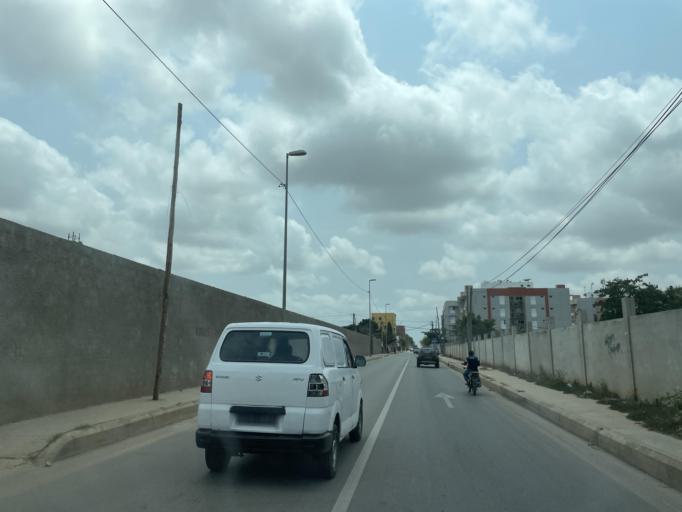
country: AO
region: Luanda
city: Luanda
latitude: -8.9408
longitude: 13.1664
